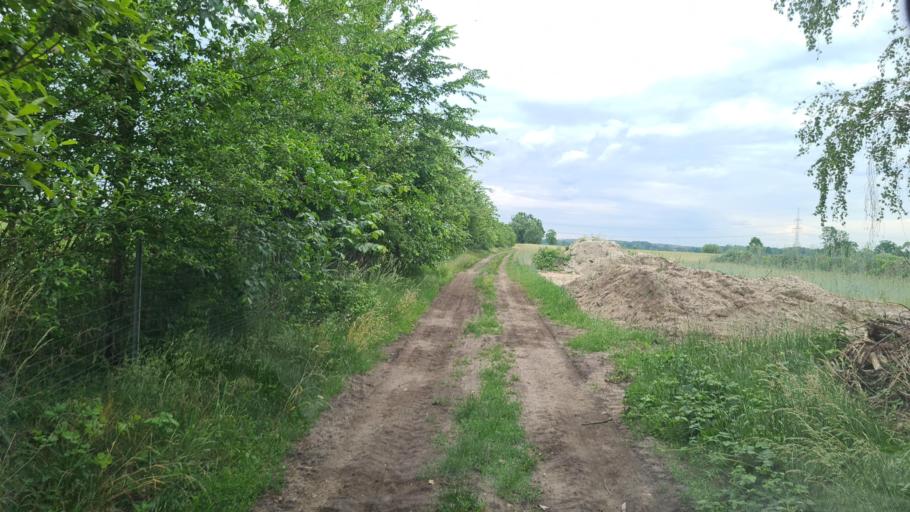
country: DE
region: Brandenburg
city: Bronkow
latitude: 51.6257
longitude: 13.9240
